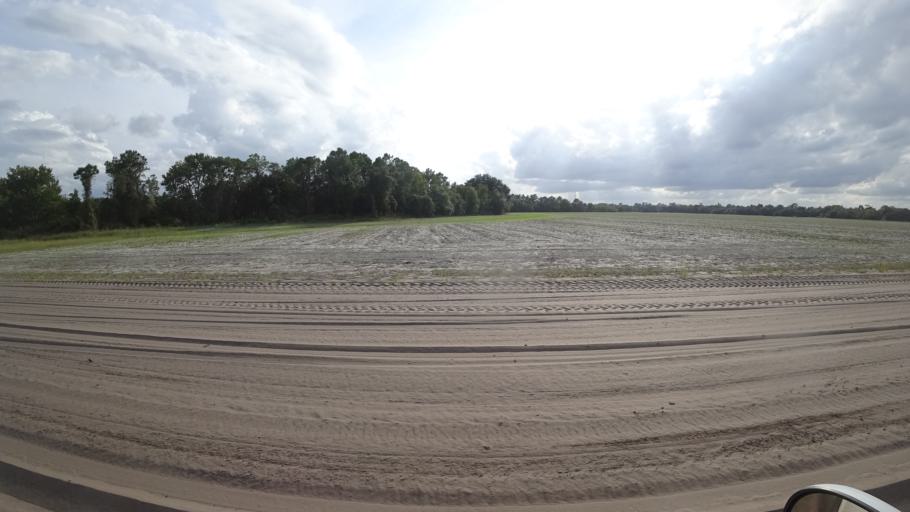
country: US
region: Florida
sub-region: Hillsborough County
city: Wimauma
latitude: 27.6071
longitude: -82.1442
